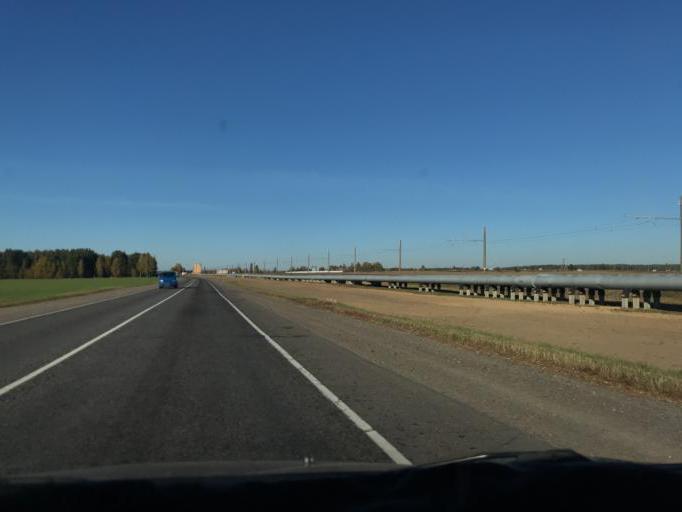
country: BY
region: Gomel
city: Mazyr
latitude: 51.9899
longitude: 29.2591
